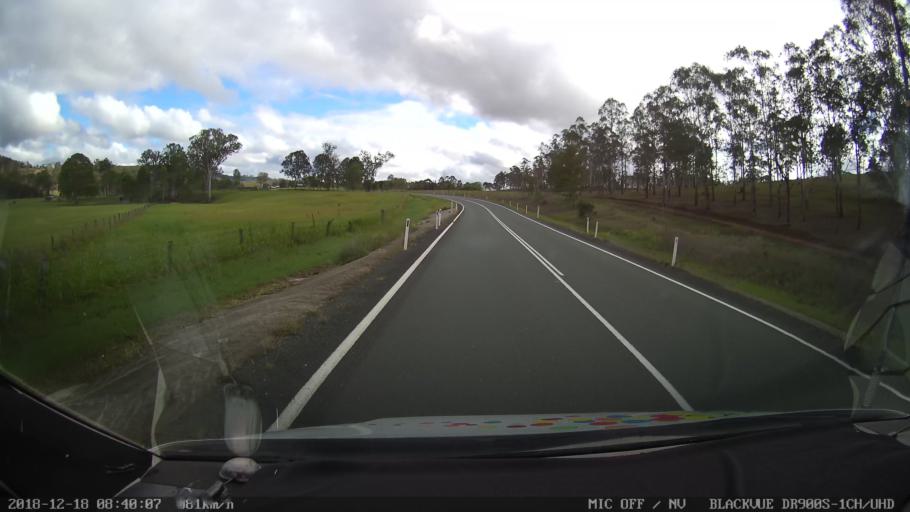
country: AU
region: Queensland
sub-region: Logan
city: Cedar Vale
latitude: -28.2455
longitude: 152.8451
